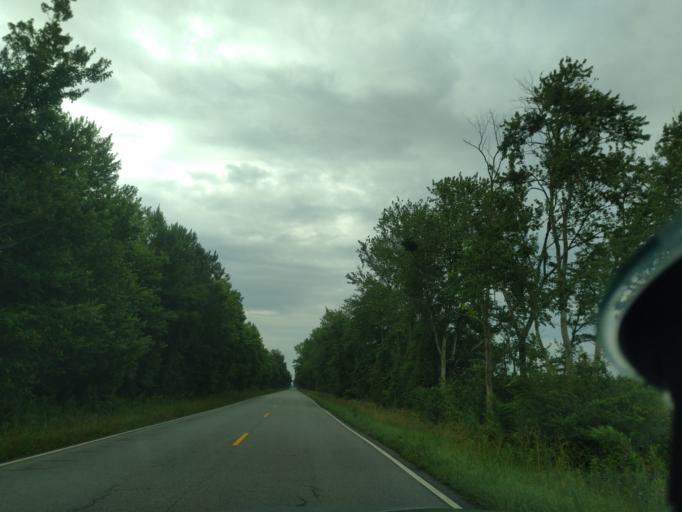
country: US
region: North Carolina
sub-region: Washington County
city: Plymouth
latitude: 35.8583
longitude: -76.5749
